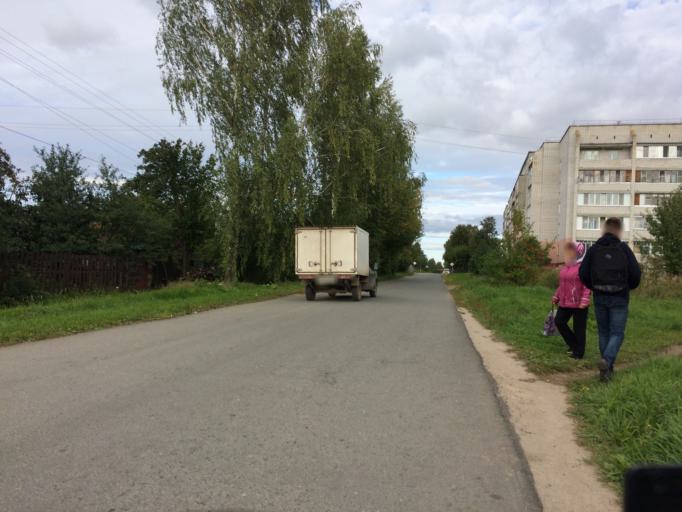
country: RU
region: Mariy-El
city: Yoshkar-Ola
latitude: 56.6577
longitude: 47.9762
